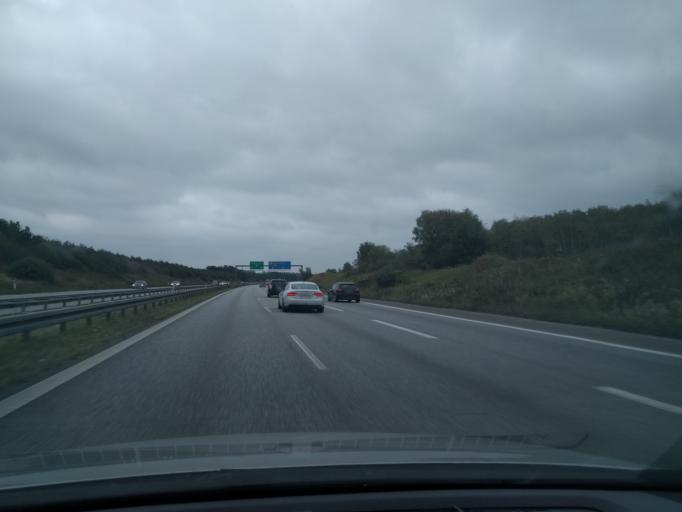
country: DK
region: Capital Region
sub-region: Frederiksberg Kommune
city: Frederiksberg
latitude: 55.6285
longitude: 12.5236
